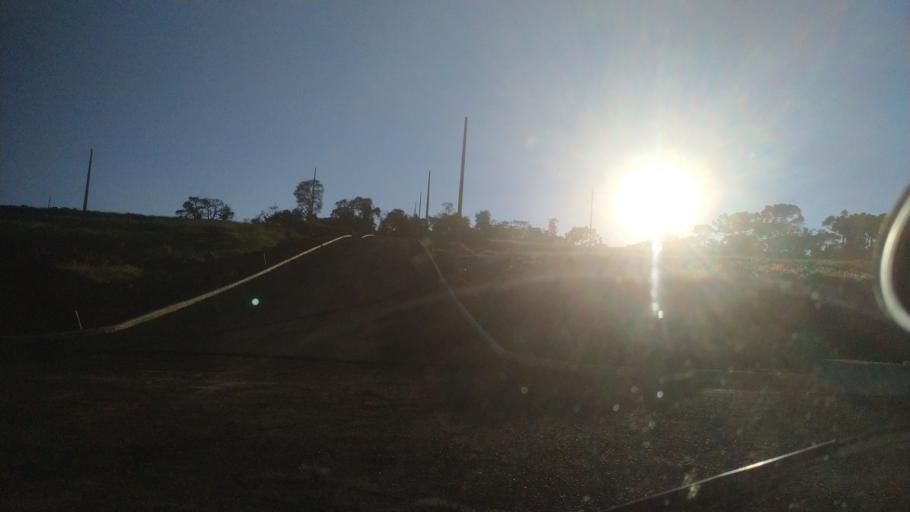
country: BR
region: Santa Catarina
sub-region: Chapeco
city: Chapeco
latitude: -27.0887
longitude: -52.6942
